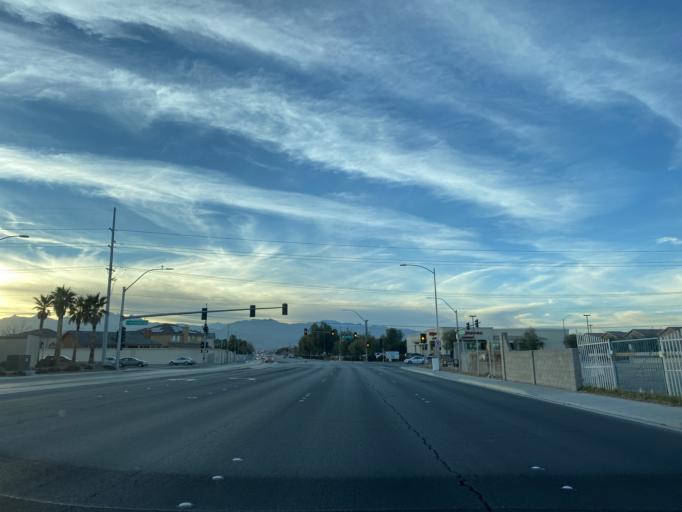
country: US
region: Nevada
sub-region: Clark County
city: Las Vegas
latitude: 36.2631
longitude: -115.2414
